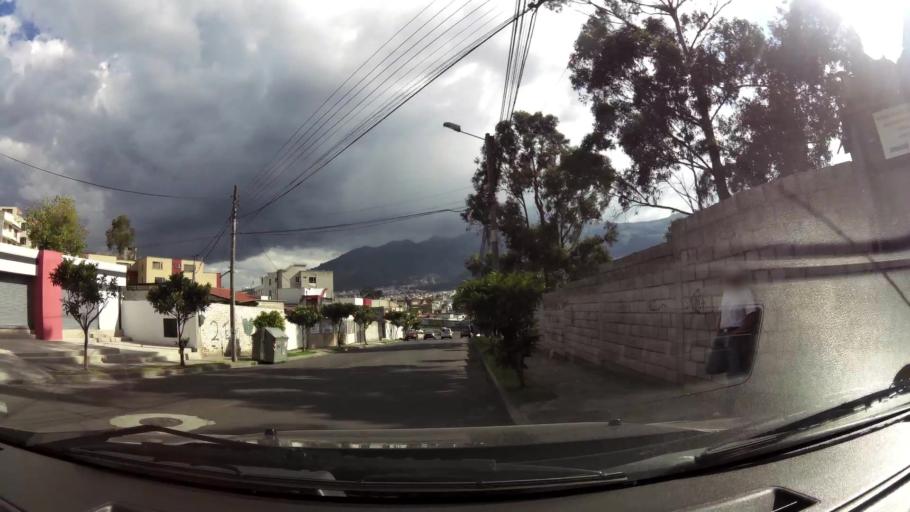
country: EC
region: Pichincha
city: Quito
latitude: -0.1105
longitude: -78.4859
